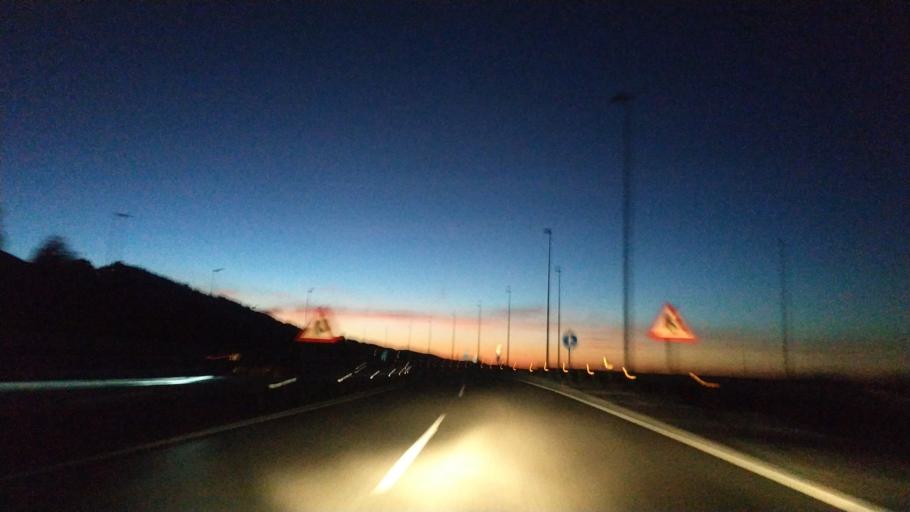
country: ES
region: Asturias
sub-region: Province of Asturias
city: Salas
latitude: 43.5492
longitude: -6.3262
